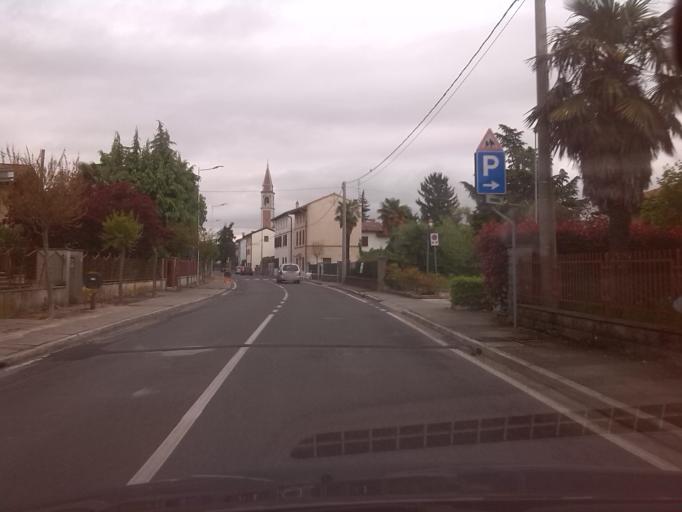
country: IT
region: Friuli Venezia Giulia
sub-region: Provincia di Gorizia
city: San Lorenzo Isontino
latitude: 45.9292
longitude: 13.5235
